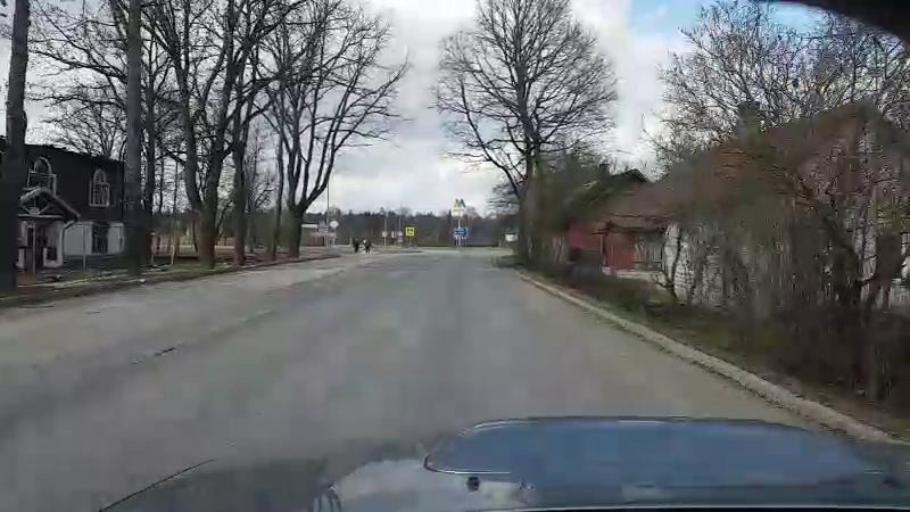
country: EE
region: Jaervamaa
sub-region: Paide linn
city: Paide
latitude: 58.8926
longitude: 25.5694
